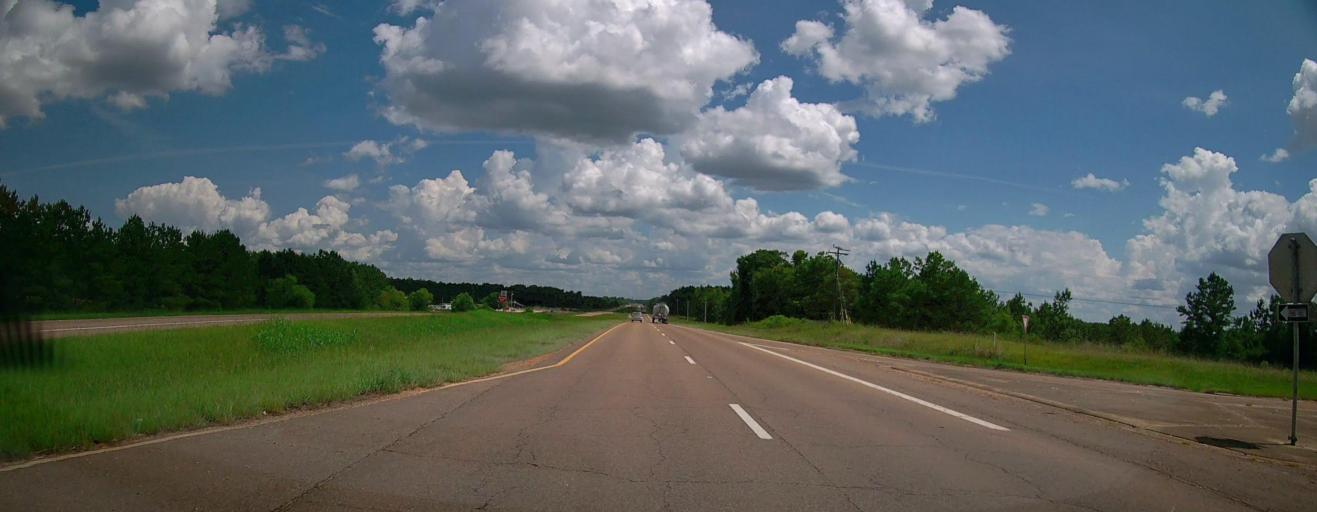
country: US
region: Mississippi
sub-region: Lowndes County
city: Columbus Air Force Base
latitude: 33.6888
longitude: -88.4378
